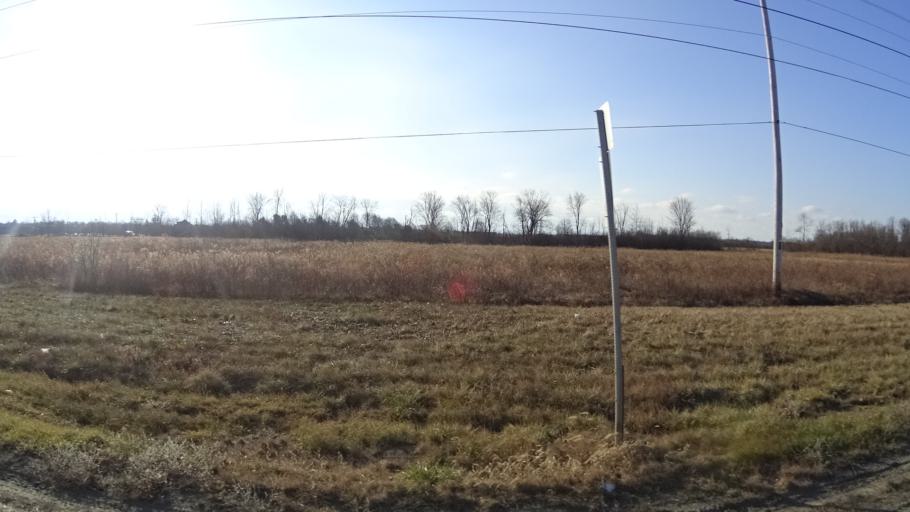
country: US
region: Ohio
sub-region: Lorain County
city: Oberlin
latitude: 41.2653
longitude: -82.2197
